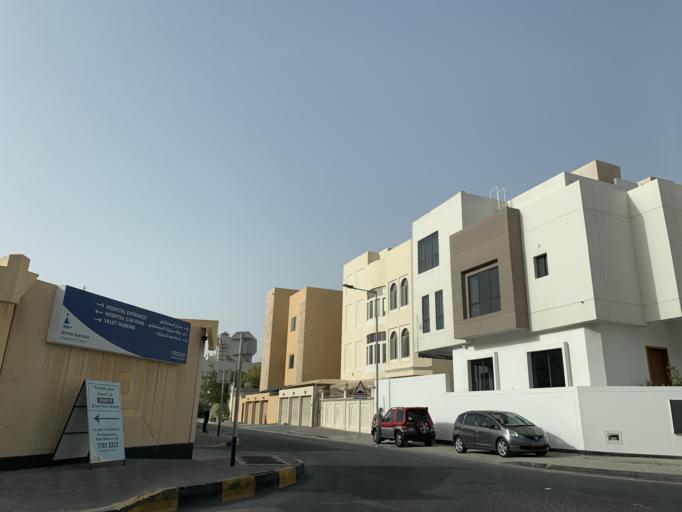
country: BH
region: Manama
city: Manama
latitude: 26.2200
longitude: 50.6142
